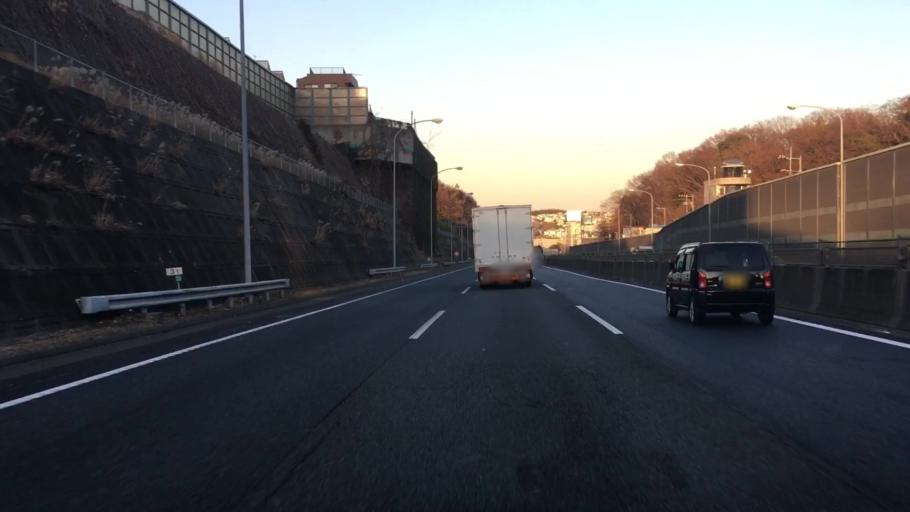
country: JP
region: Kanagawa
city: Yokohama
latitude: 35.4570
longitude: 139.5834
